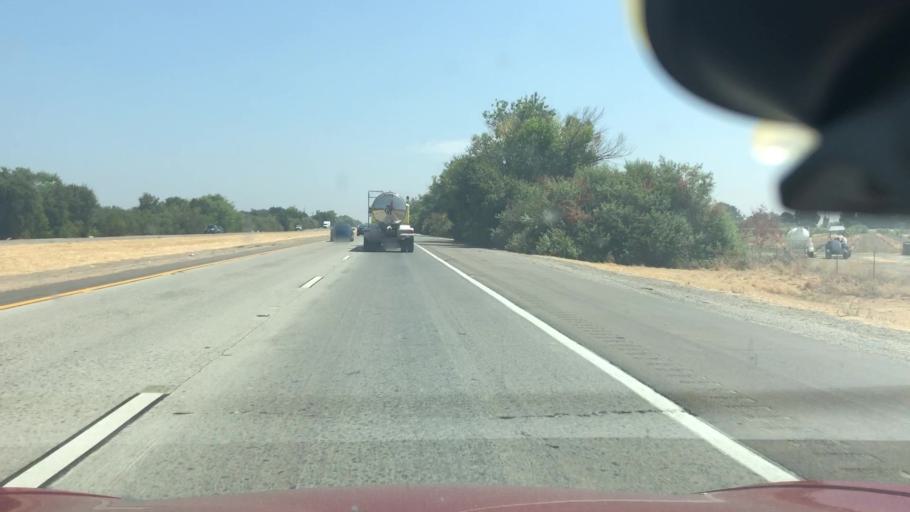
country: US
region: California
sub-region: San Joaquin County
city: Thornton
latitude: 38.2088
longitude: -121.4188
